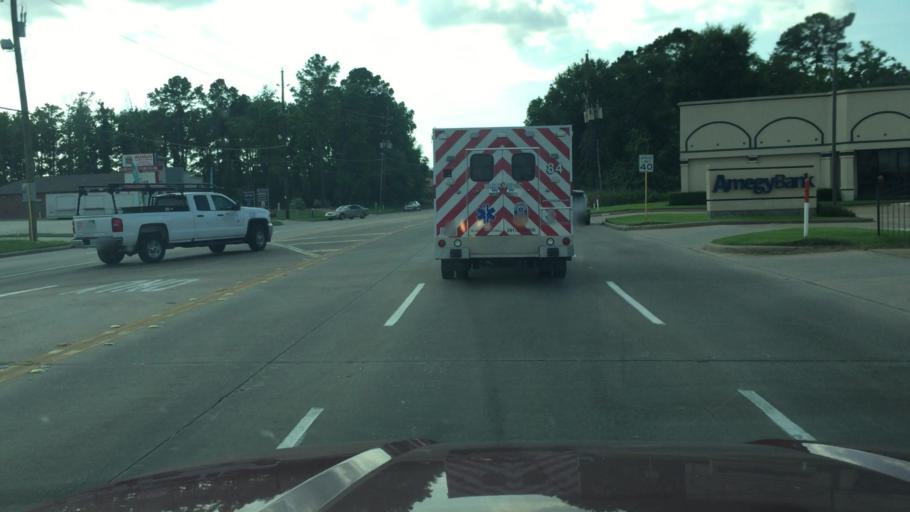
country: US
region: Texas
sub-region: Harris County
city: Tomball
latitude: 30.0233
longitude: -95.5266
